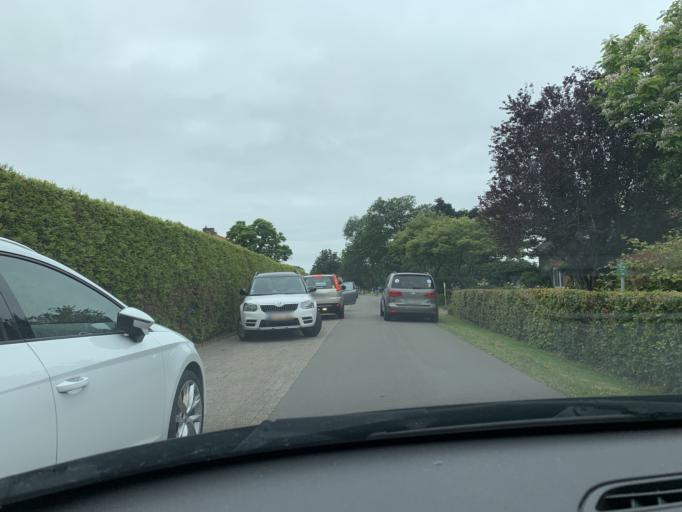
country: DE
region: Lower Saxony
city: Westerstede
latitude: 53.2437
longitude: 7.9024
